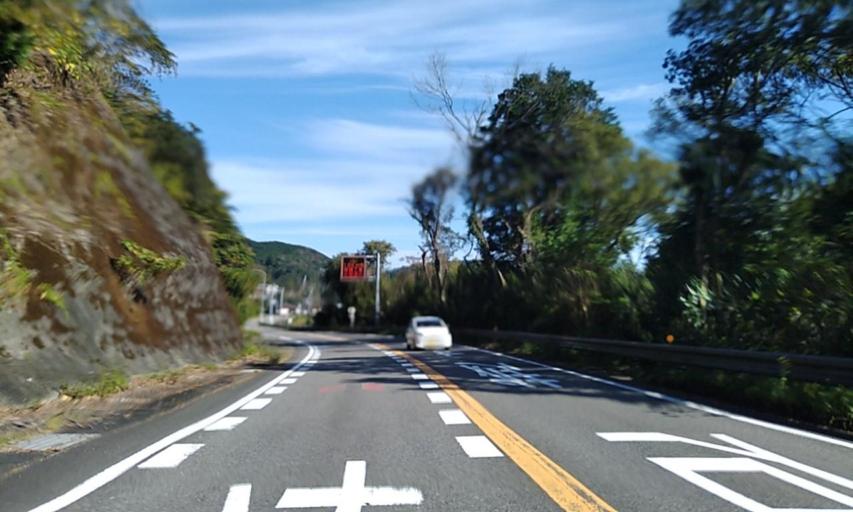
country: JP
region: Mie
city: Owase
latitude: 34.1601
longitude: 136.2742
